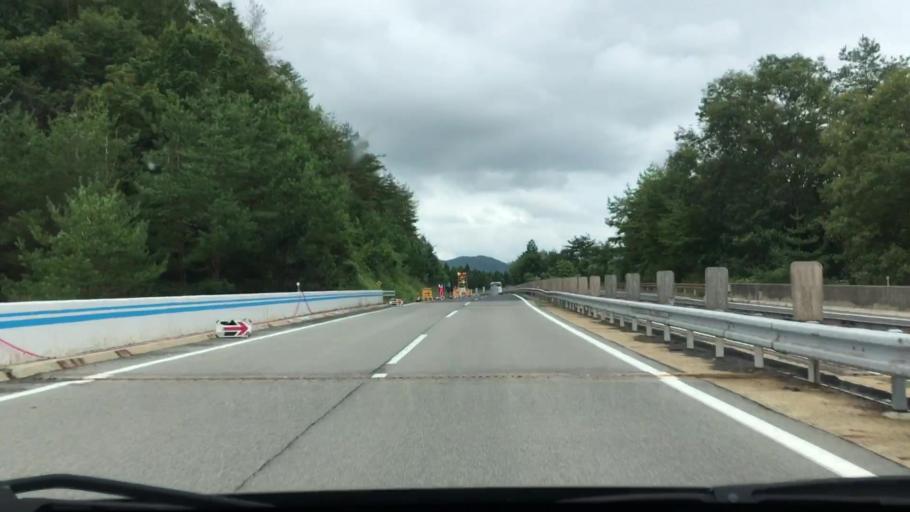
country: JP
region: Hiroshima
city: Miyoshi
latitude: 34.7348
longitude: 132.7093
